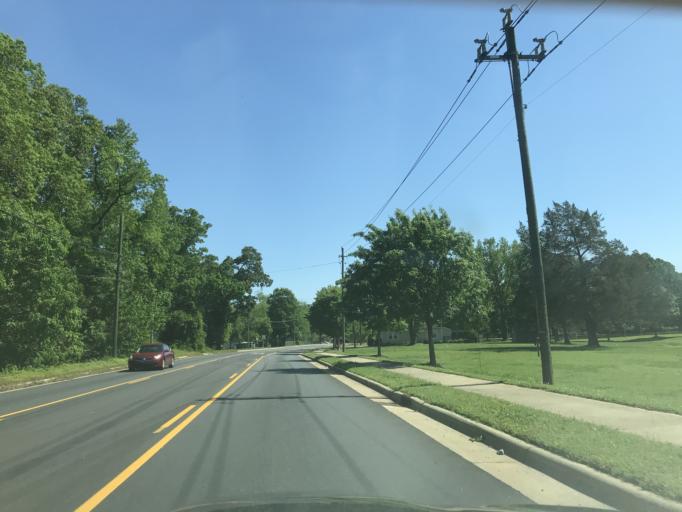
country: US
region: North Carolina
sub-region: Wake County
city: Garner
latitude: 35.7363
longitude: -78.6285
